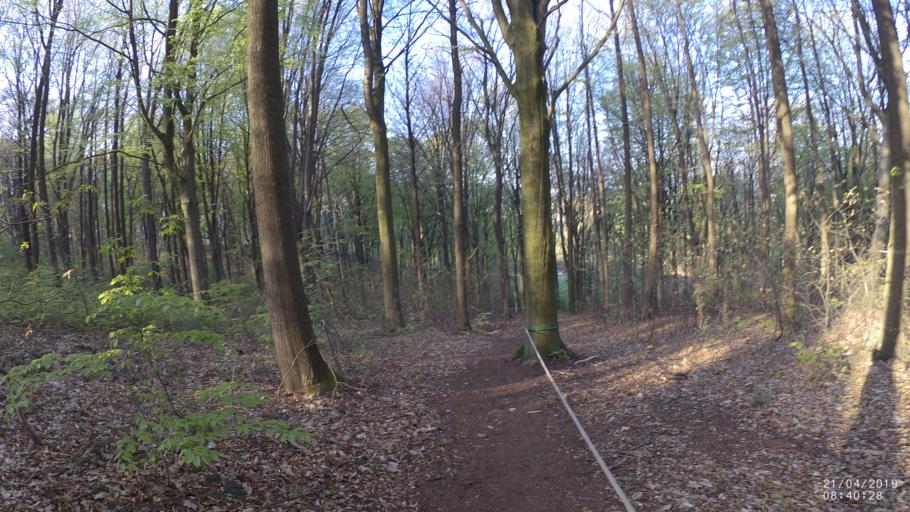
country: BE
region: Flanders
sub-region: Provincie Vlaams-Brabant
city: Lubbeek
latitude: 50.9157
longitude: 4.8484
